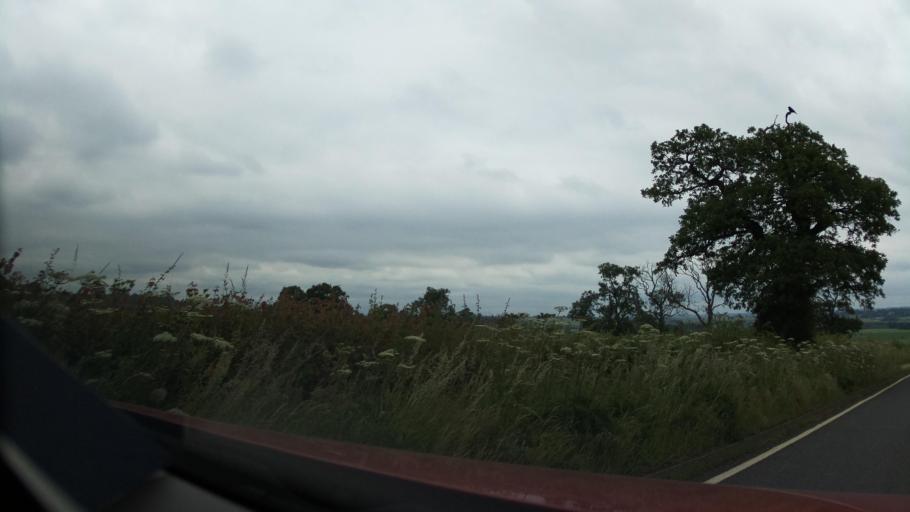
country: GB
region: England
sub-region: Leicestershire
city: Melton Mowbray
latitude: 52.7198
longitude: -0.8332
